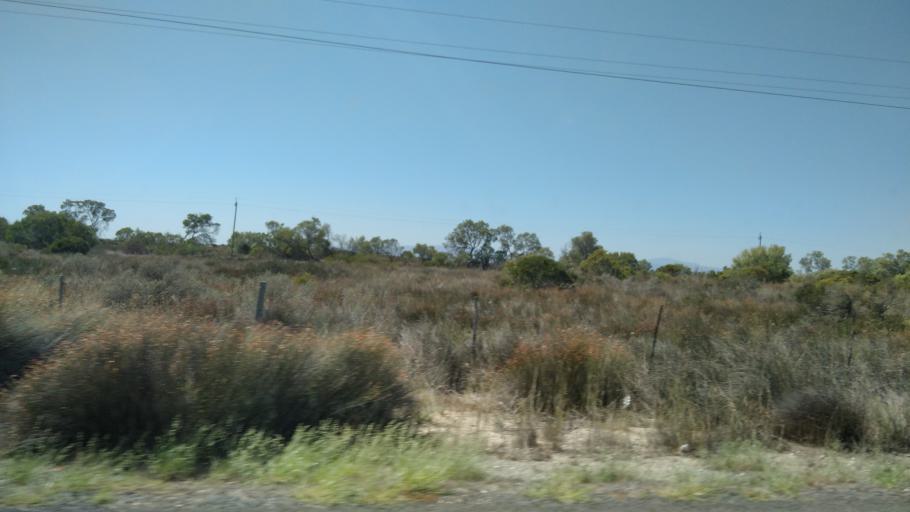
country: ZA
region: Western Cape
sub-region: West Coast District Municipality
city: Vredenburg
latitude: -33.0240
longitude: 18.2732
